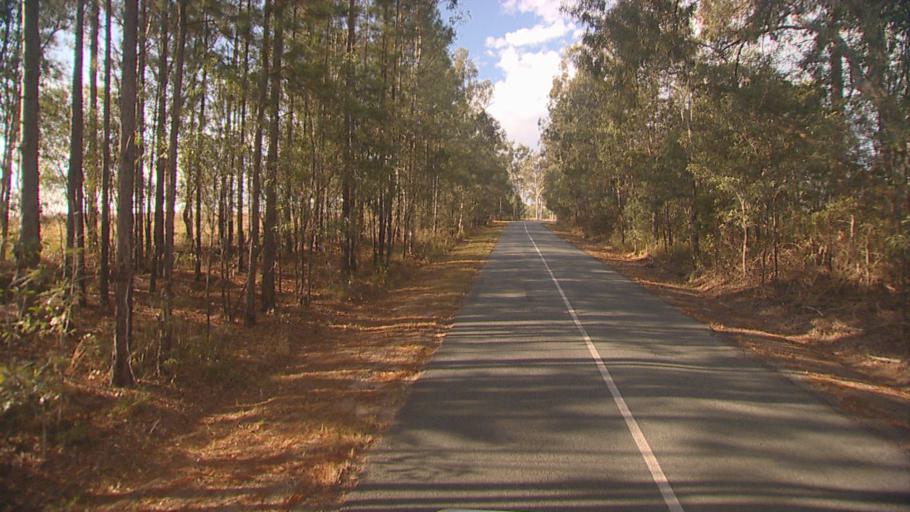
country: AU
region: Queensland
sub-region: Logan
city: Chambers Flat
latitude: -27.8479
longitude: 153.1397
